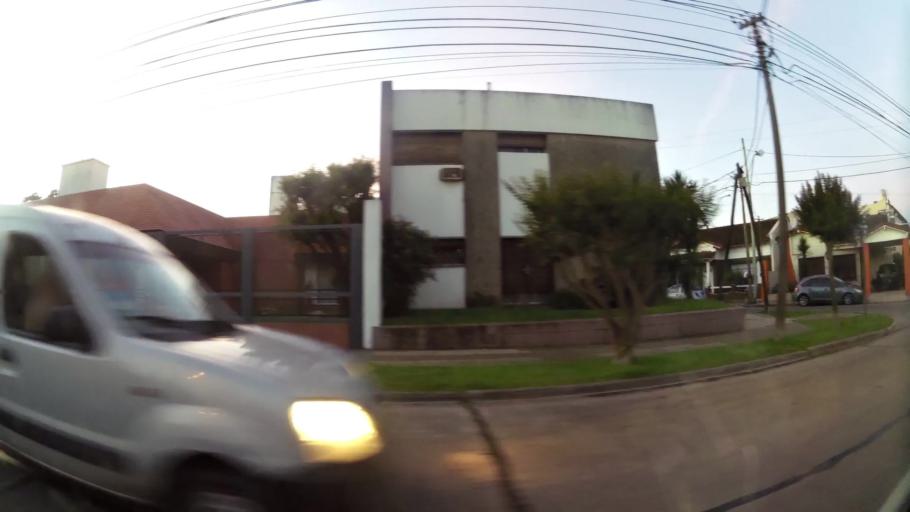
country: AR
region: Buenos Aires
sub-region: Partido de Moron
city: Moron
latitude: -34.6542
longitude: -58.6348
